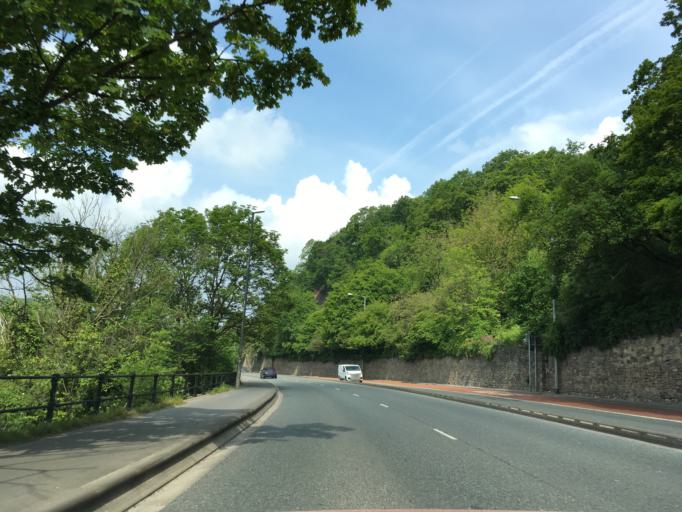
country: GB
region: England
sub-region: Bristol
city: Bristol
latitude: 51.4695
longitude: -2.6365
